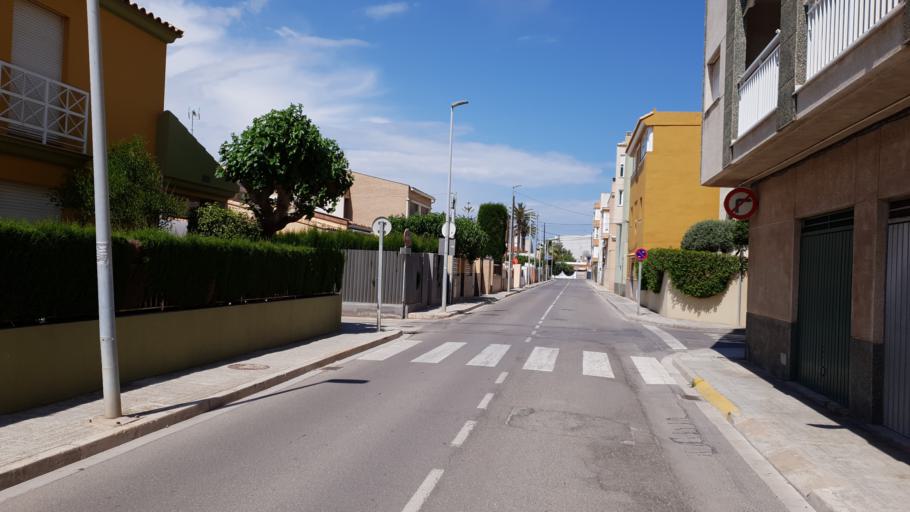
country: ES
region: Valencia
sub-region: Provincia de Castello
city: Burriana
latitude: 39.8631
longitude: -0.0778
